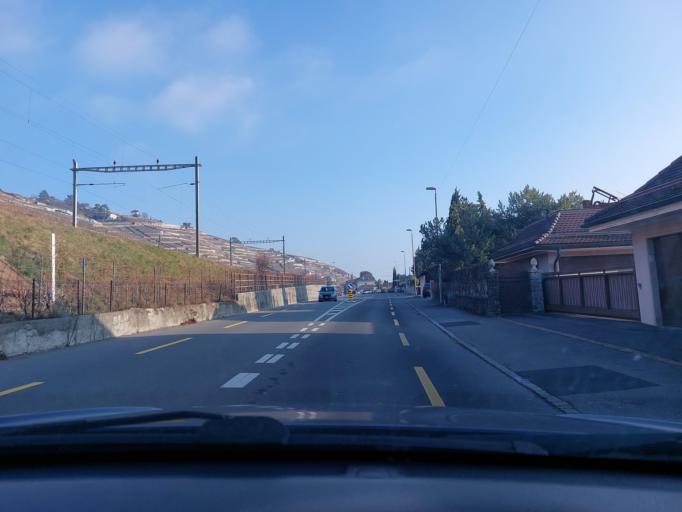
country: CH
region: Vaud
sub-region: Lavaux-Oron District
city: Lutry
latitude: 46.4969
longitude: 6.7040
